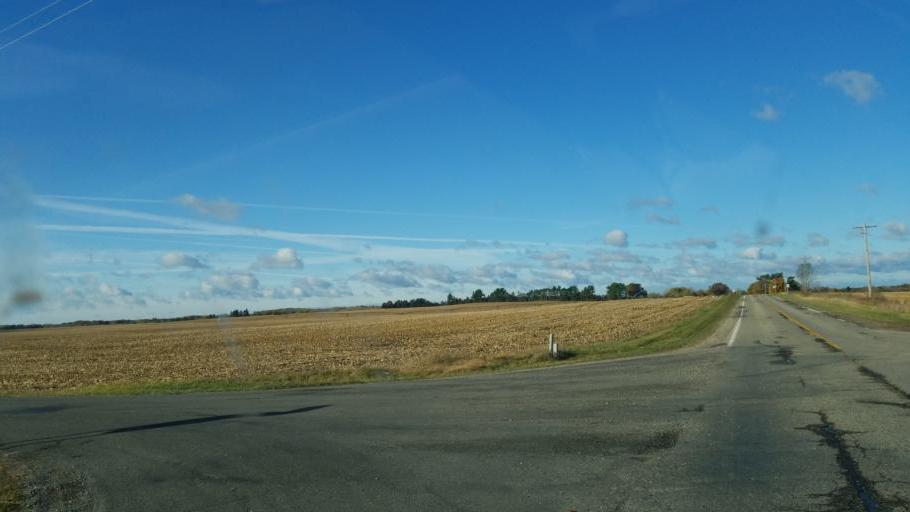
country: US
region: Michigan
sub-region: Montcalm County
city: Edmore
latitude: 43.4663
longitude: -85.1045
